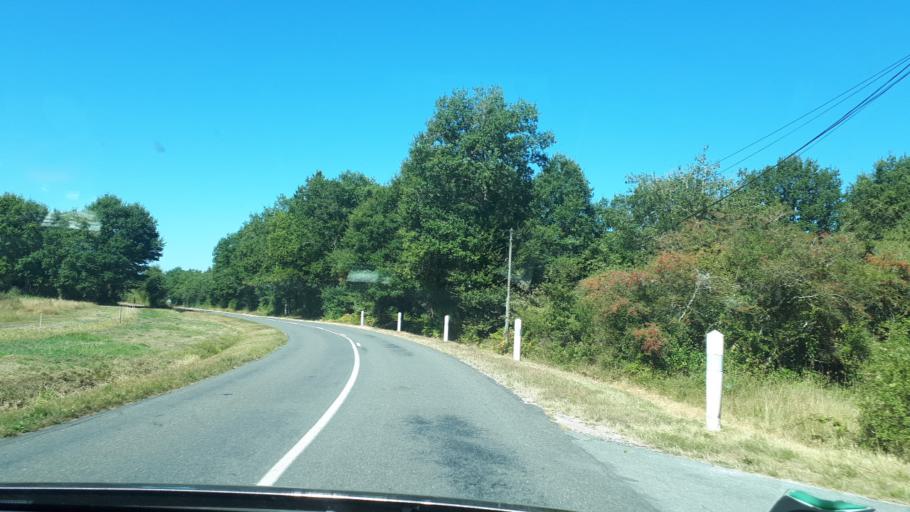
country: FR
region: Centre
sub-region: Departement du Loiret
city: Cerdon
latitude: 47.6418
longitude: 2.4010
